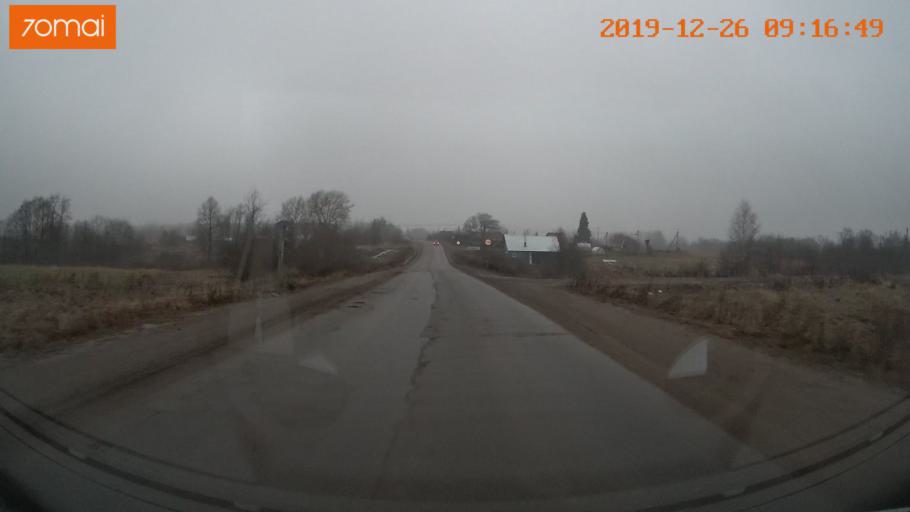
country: RU
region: Vologda
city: Gryazovets
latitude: 58.9230
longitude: 40.2393
